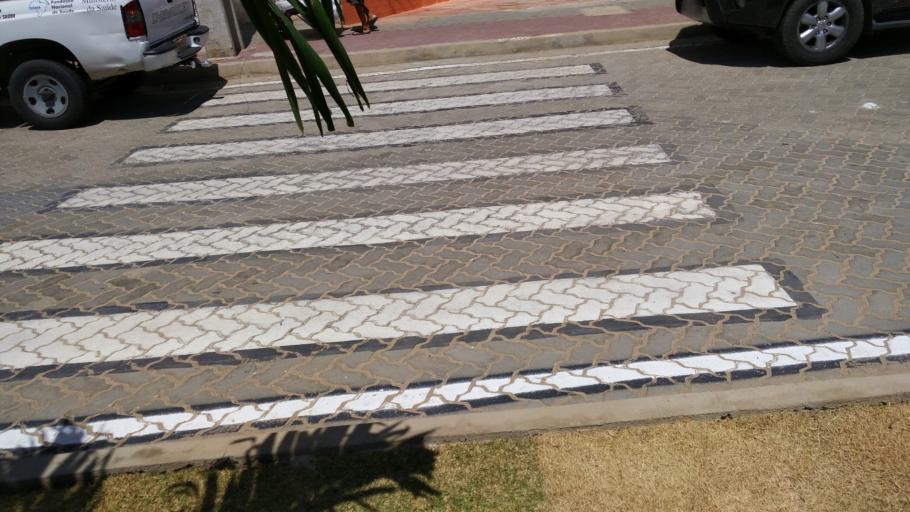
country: BR
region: Ceara
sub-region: Fortaleza
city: Fortaleza
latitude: -3.7641
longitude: -38.5092
